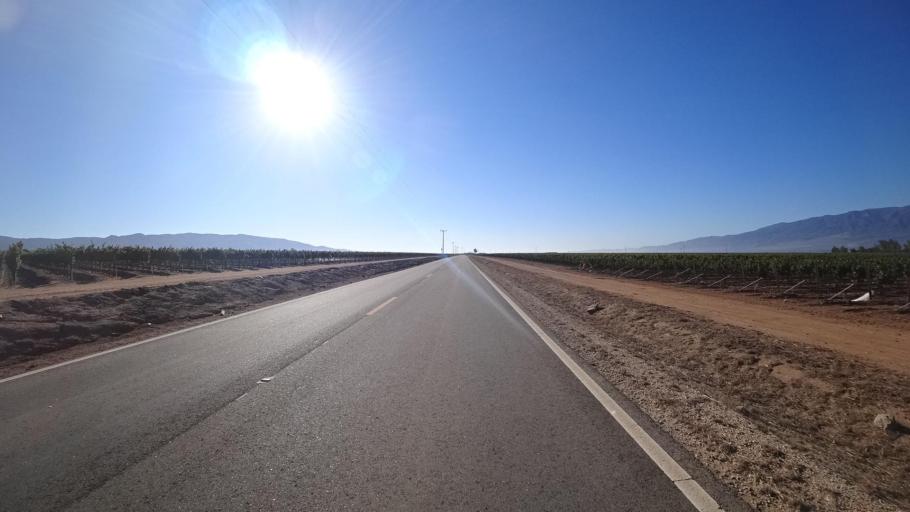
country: US
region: California
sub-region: Monterey County
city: Gonzales
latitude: 36.5057
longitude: -121.4002
